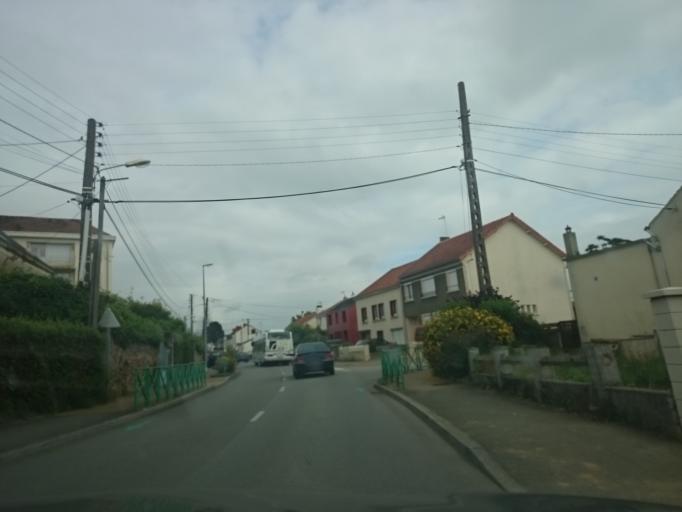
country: FR
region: Pays de la Loire
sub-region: Departement de la Loire-Atlantique
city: La Montagne
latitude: 47.1867
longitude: -1.6854
